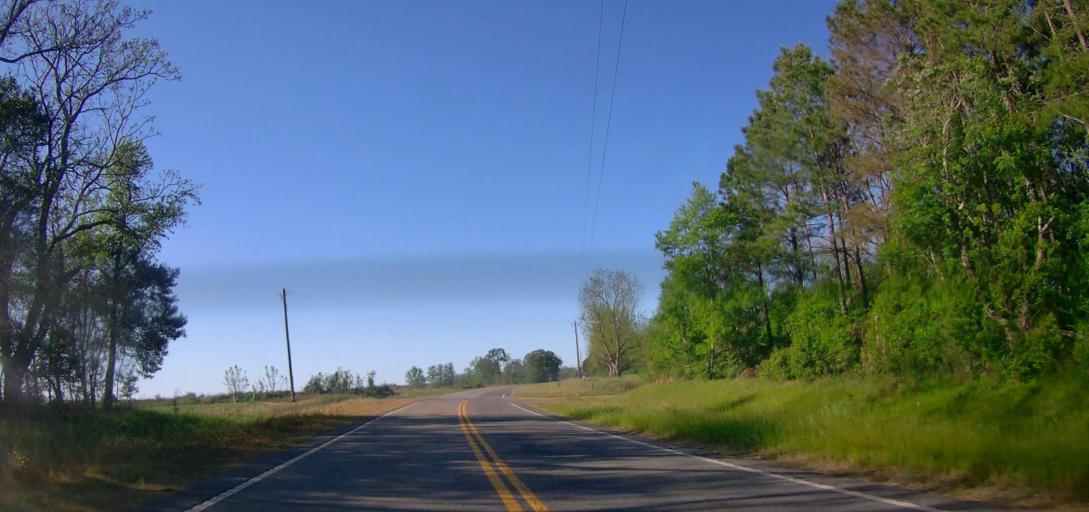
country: US
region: Georgia
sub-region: Ben Hill County
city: Fitzgerald
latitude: 31.7057
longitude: -83.3098
